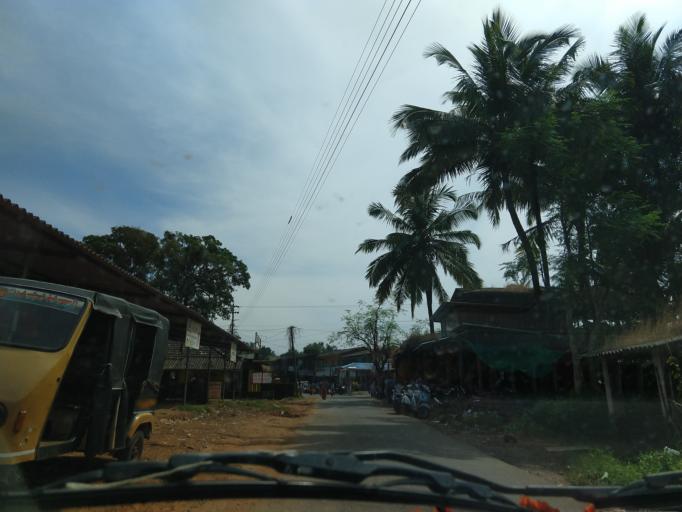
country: IN
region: Maharashtra
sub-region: Sindhudurg
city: Savantvadi
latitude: 15.9705
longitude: 73.7726
